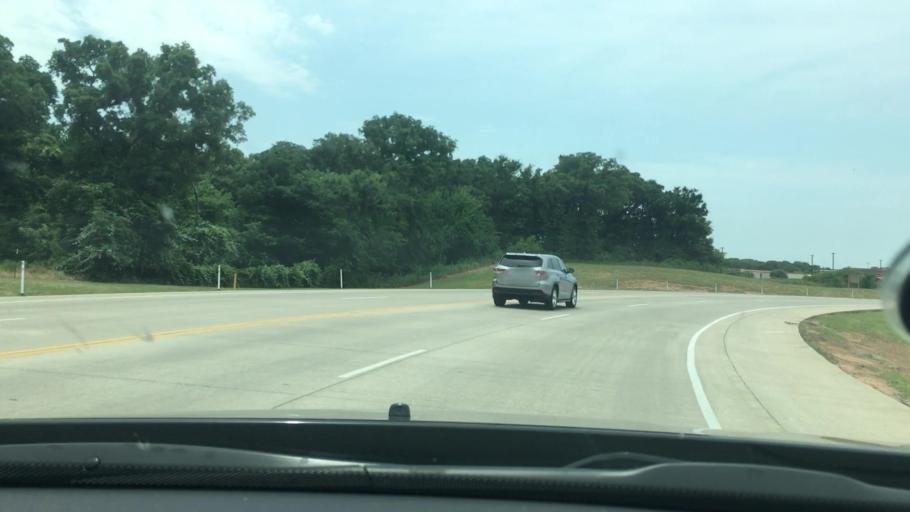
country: US
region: Texas
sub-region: Cooke County
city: Gainesville
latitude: 33.7376
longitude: -97.1421
